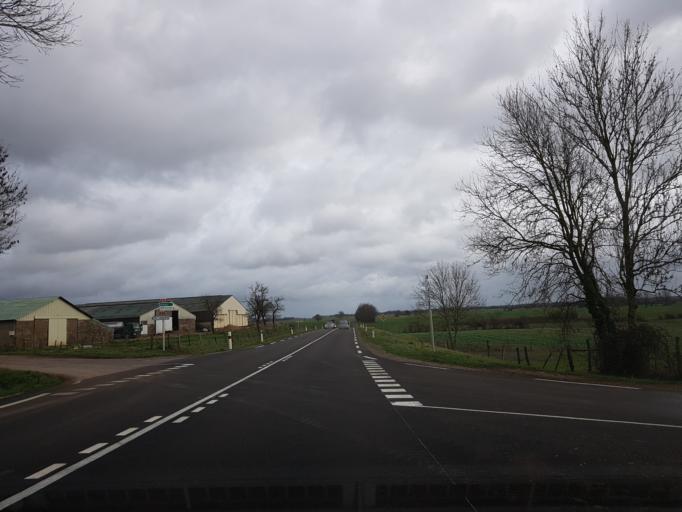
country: FR
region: Champagne-Ardenne
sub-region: Departement de la Haute-Marne
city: Chalindrey
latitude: 47.8498
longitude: 5.4148
